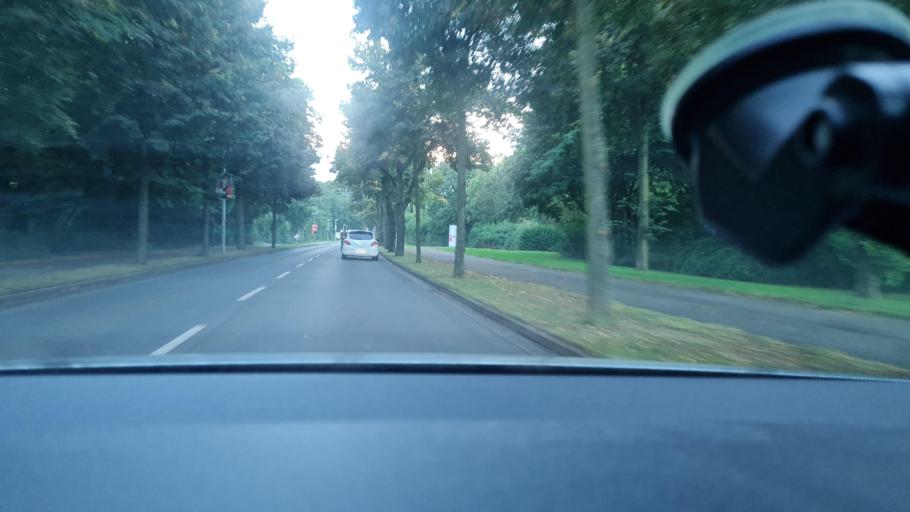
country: DE
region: North Rhine-Westphalia
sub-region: Regierungsbezirk Dusseldorf
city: Moers
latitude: 51.4823
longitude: 6.6197
